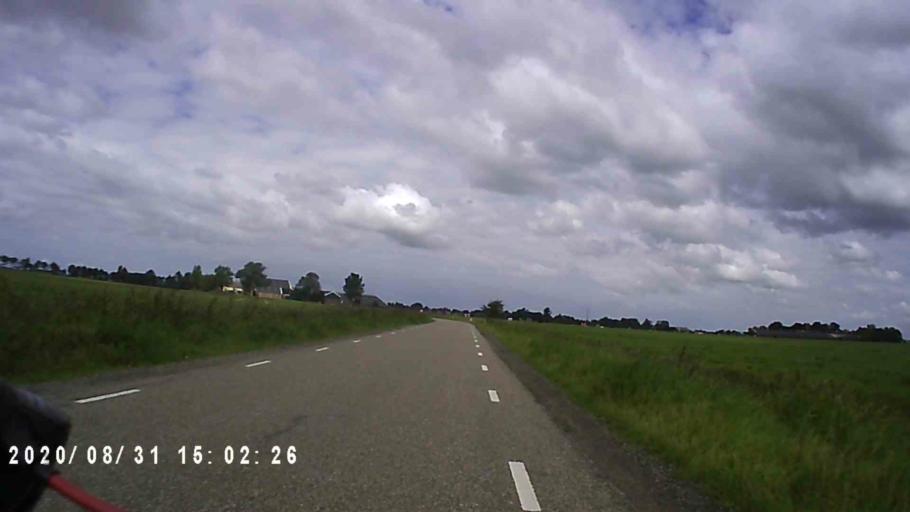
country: NL
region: Groningen
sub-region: Gemeente Zuidhorn
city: Oldehove
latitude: 53.2904
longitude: 6.3921
